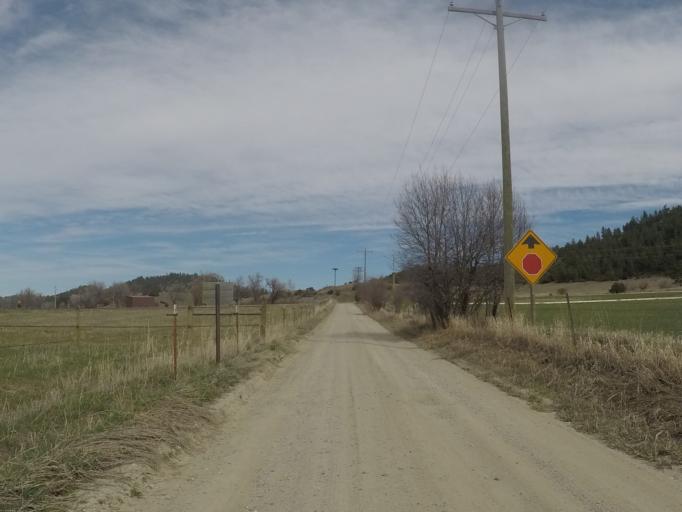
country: US
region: Montana
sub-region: Stillwater County
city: Columbus
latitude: 45.5803
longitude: -109.3262
